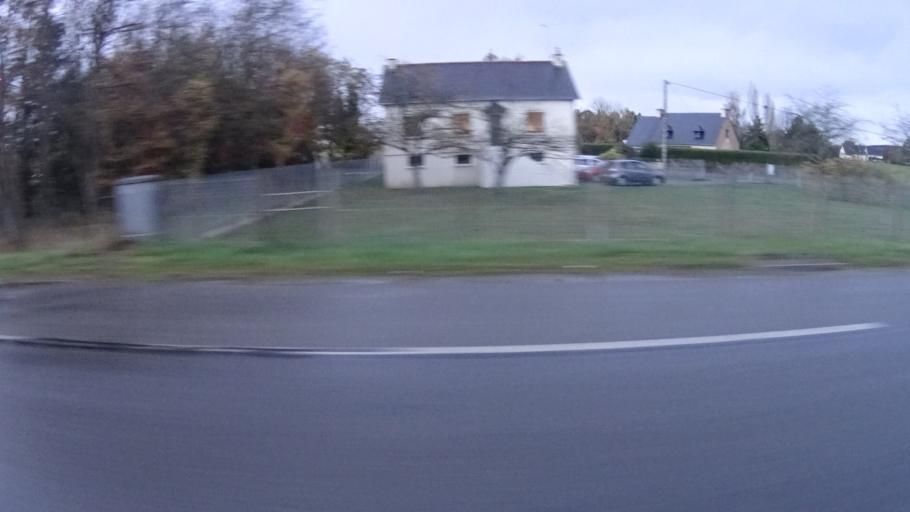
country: FR
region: Brittany
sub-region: Departement d'Ille-et-Vilaine
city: Bains-sur-Oust
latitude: 47.6808
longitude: -2.0596
